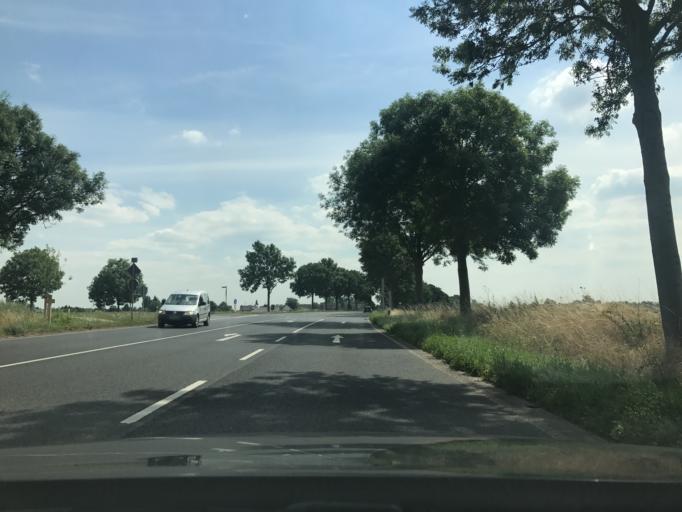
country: DE
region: North Rhine-Westphalia
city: Tonisvorst
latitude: 51.3959
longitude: 6.4962
